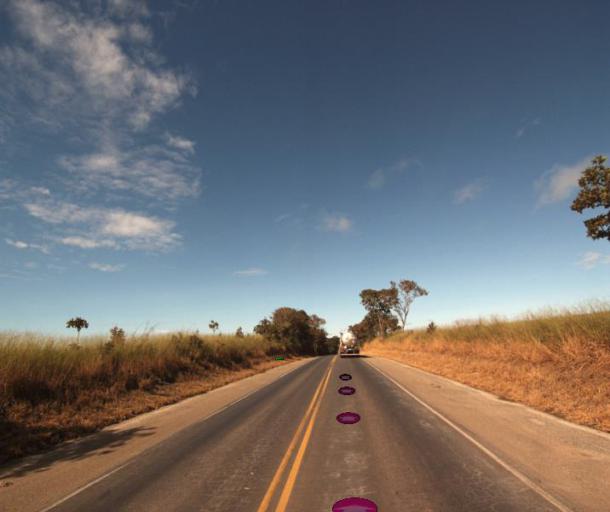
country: BR
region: Goias
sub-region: Itapaci
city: Itapaci
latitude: -14.8442
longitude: -49.3127
